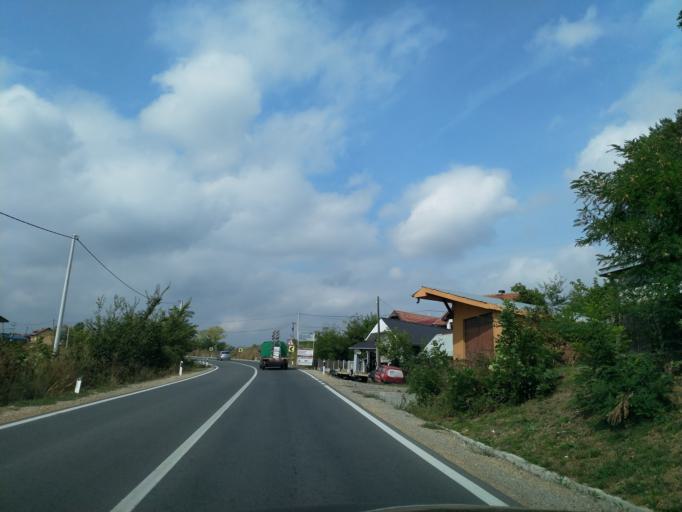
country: RS
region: Central Serbia
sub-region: Sumadijski Okrug
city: Kragujevac
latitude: 44.0613
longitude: 20.8902
